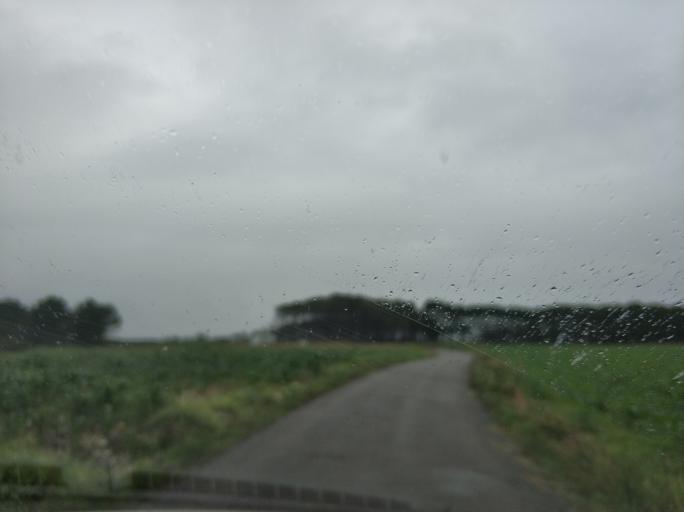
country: ES
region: Asturias
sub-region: Province of Asturias
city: Tineo
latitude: 43.5635
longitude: -6.4697
